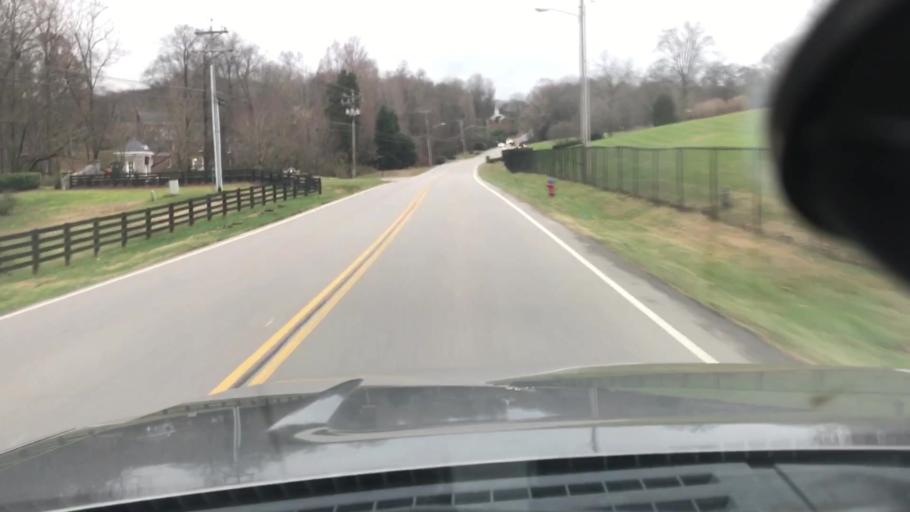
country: US
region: Tennessee
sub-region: Williamson County
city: Brentwood Estates
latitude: 35.9838
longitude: -86.7415
